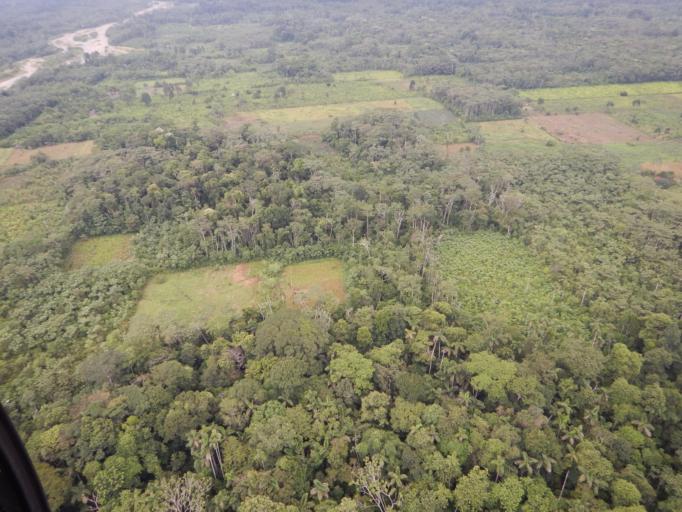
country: BO
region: Cochabamba
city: Chimore
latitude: -17.2208
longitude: -64.7030
